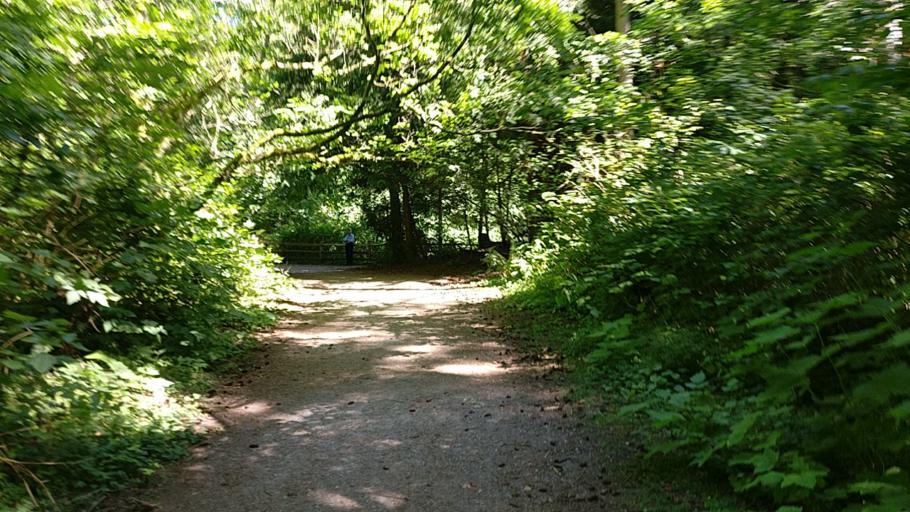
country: CA
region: British Columbia
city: Surrey
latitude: 49.0499
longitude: -122.8626
